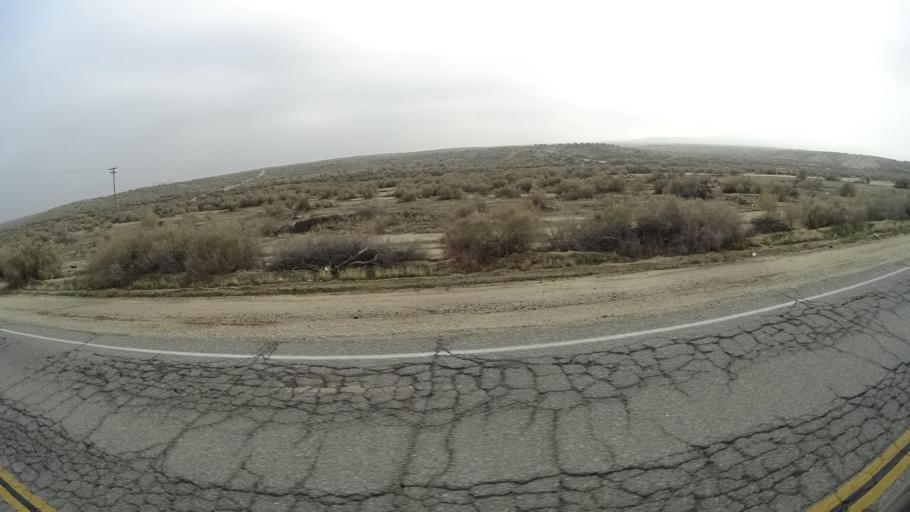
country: US
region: California
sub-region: Kern County
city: South Taft
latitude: 35.1364
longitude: -119.4106
